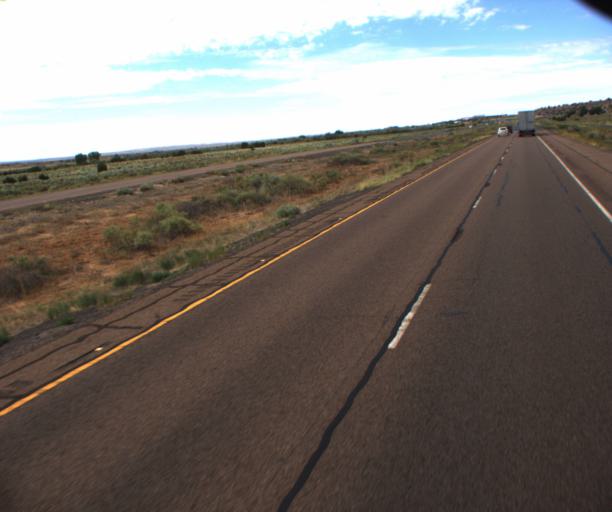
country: US
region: Arizona
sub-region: Apache County
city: Houck
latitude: 35.1706
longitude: -109.4770
